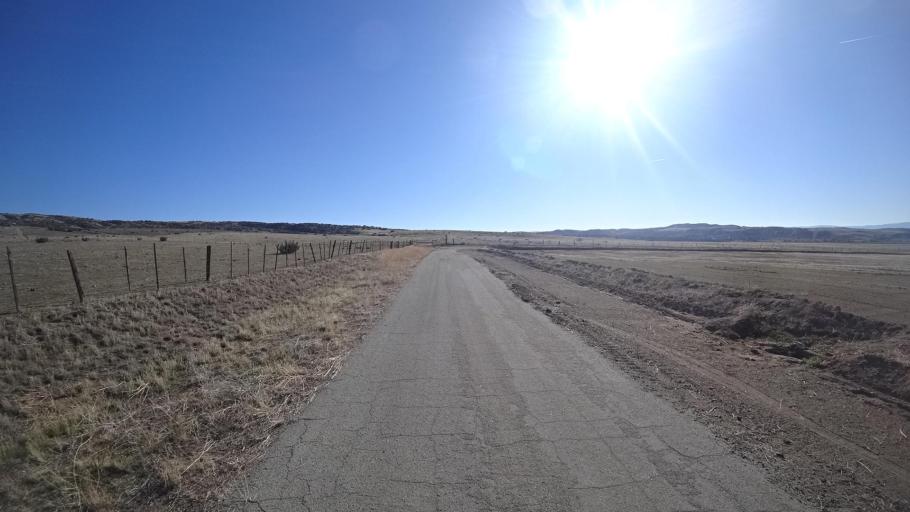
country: US
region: California
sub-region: Kern County
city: Maricopa
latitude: 34.9393
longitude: -119.4555
